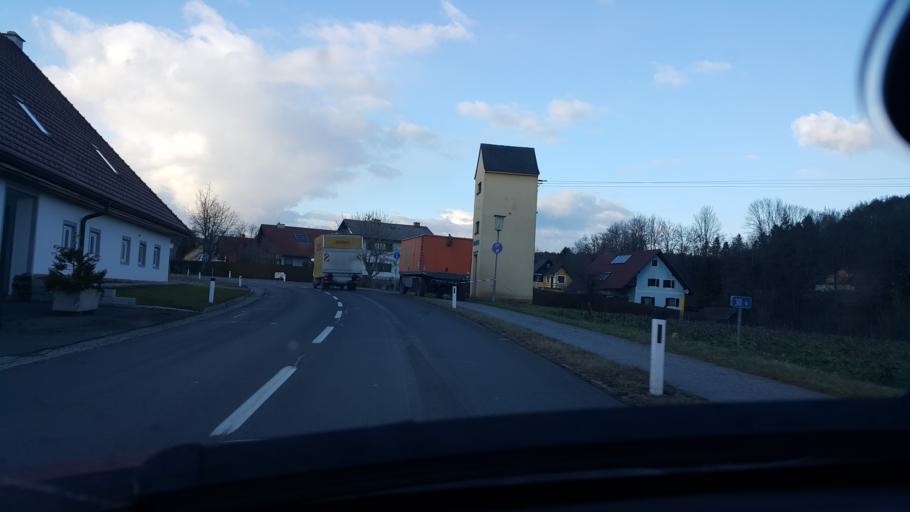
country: AT
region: Styria
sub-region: Politischer Bezirk Deutschlandsberg
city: Hollenegg
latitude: 46.7849
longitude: 15.2404
